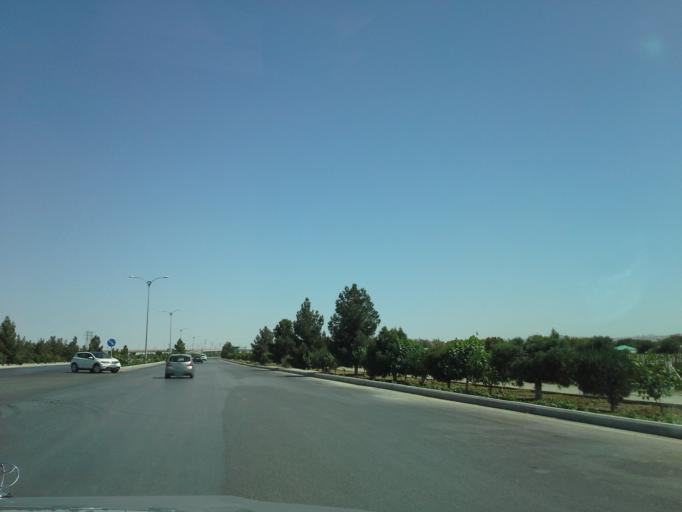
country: TM
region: Ahal
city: Annau
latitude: 37.9157
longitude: 58.4733
